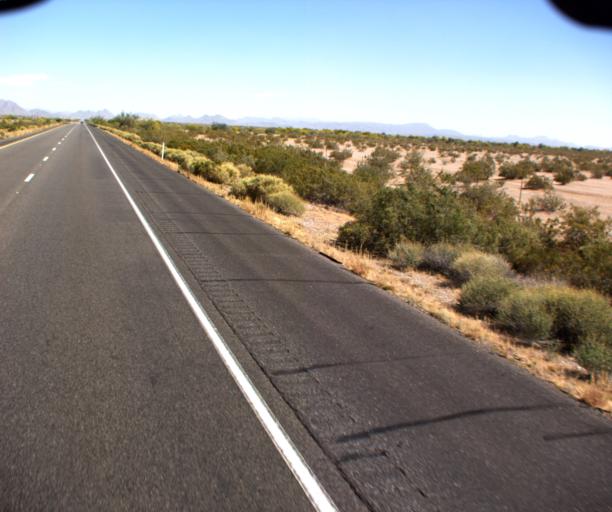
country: US
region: Arizona
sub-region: Maricopa County
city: Gila Bend
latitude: 32.9336
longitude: -112.7100
